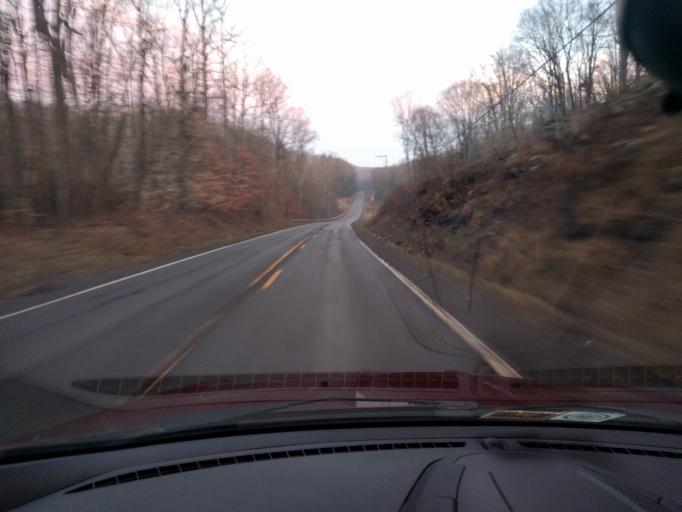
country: US
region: West Virginia
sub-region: Greenbrier County
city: Rainelle
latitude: 38.0285
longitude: -80.9151
